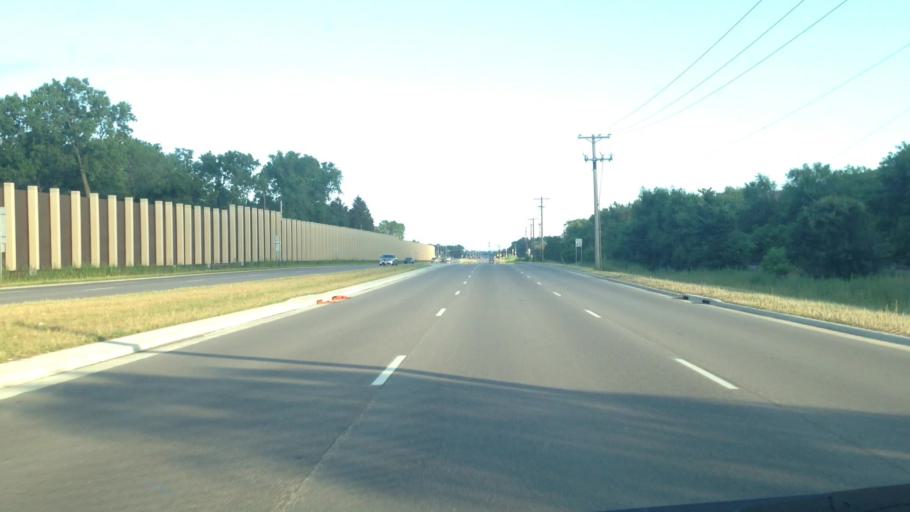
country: US
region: Minnesota
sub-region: Hennepin County
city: Brooklyn Park
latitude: 45.0756
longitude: -93.3722
